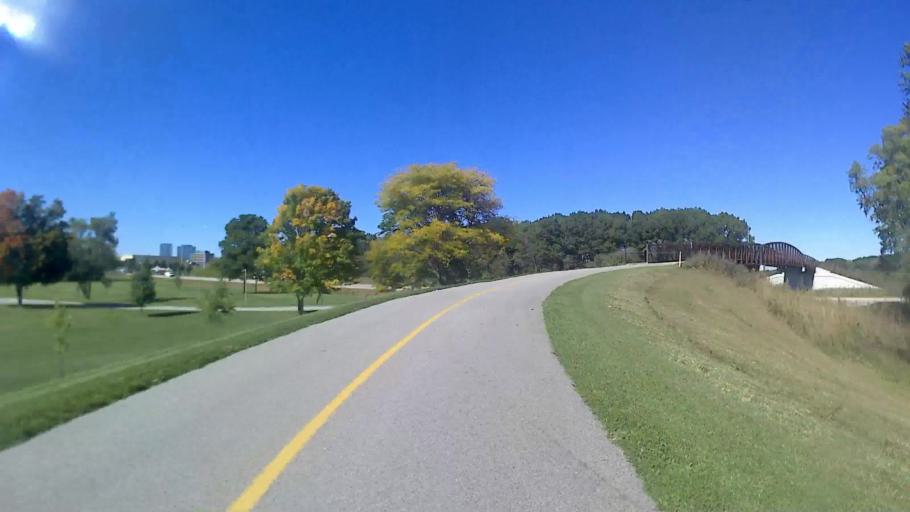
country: US
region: Illinois
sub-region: Cook County
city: Rolling Meadows
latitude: 42.0347
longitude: -88.0255
